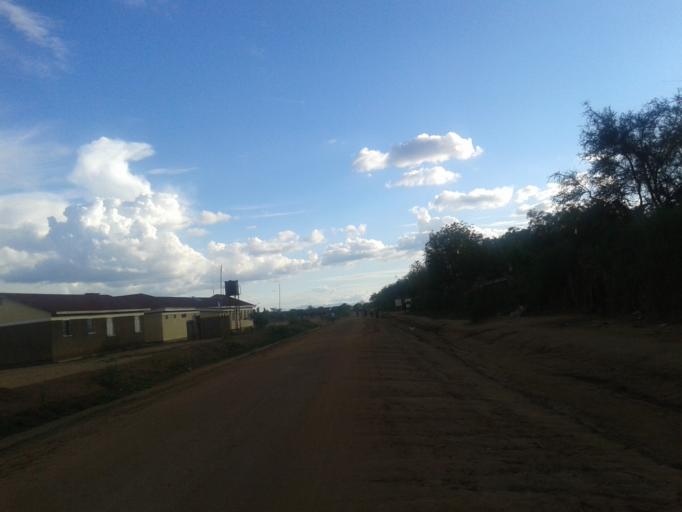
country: UG
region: Northern Region
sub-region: Kotido District
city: Kotido
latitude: 3.0027
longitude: 34.1106
